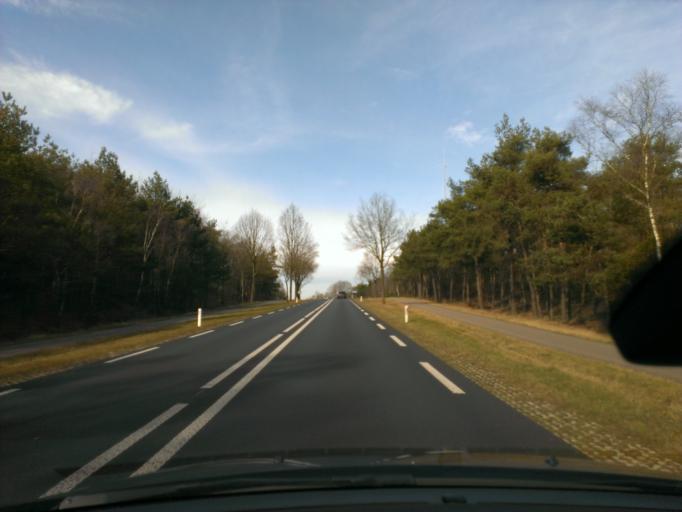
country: NL
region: Gelderland
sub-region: Gemeente Oldebroek
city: Oldebroek
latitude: 52.3846
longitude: 5.9112
